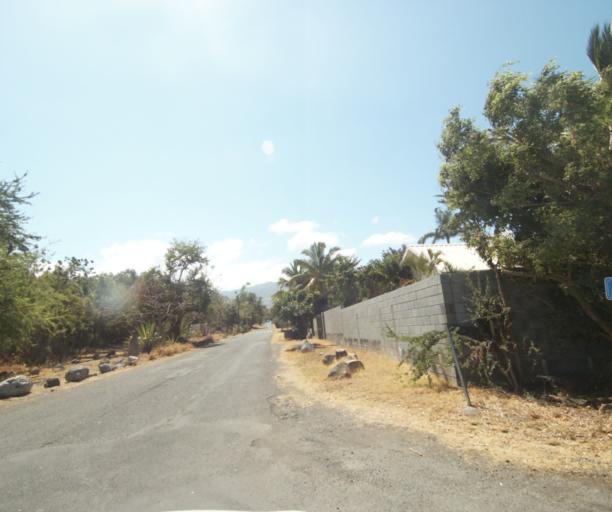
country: RE
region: Reunion
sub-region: Reunion
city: Le Port
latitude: -20.9616
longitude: 55.3011
